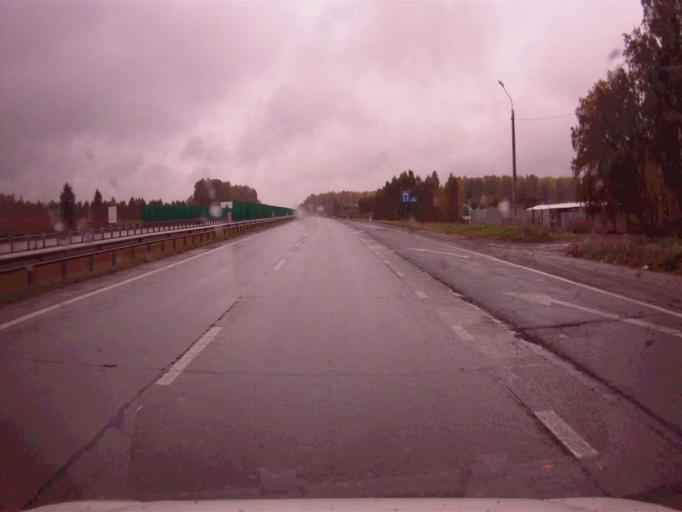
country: RU
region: Chelyabinsk
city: Dolgoderevenskoye
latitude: 55.3275
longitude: 61.3263
